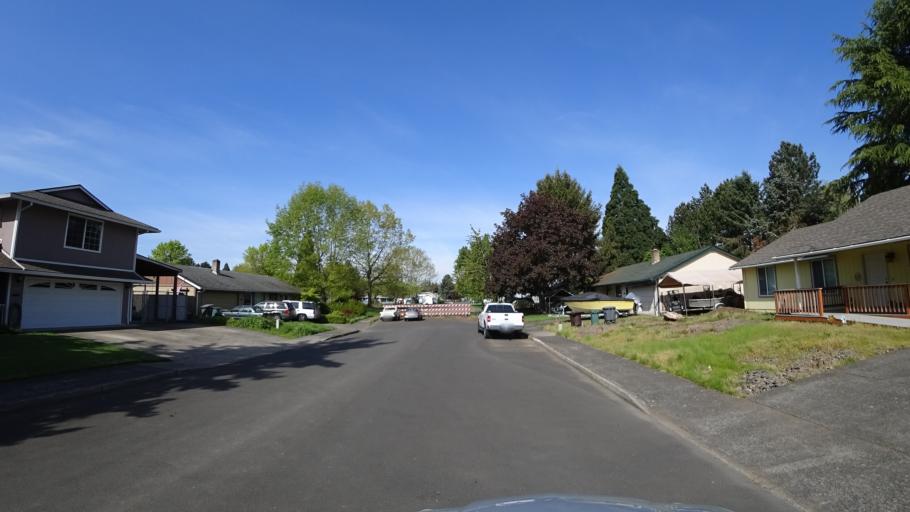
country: US
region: Oregon
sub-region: Washington County
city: Hillsboro
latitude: 45.5226
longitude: -122.9483
